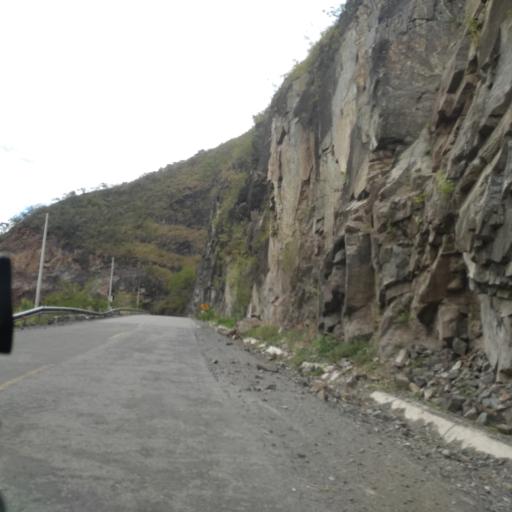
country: PE
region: Cajamarca
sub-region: Provincia de San Ignacio
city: Chirinos
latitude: -5.2394
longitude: -78.8556
